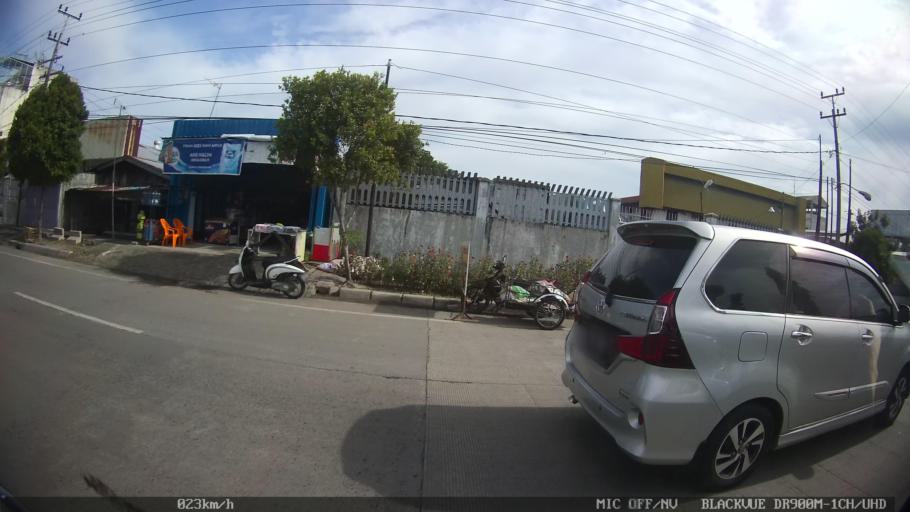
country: ID
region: North Sumatra
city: Medan
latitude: 3.6295
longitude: 98.6851
